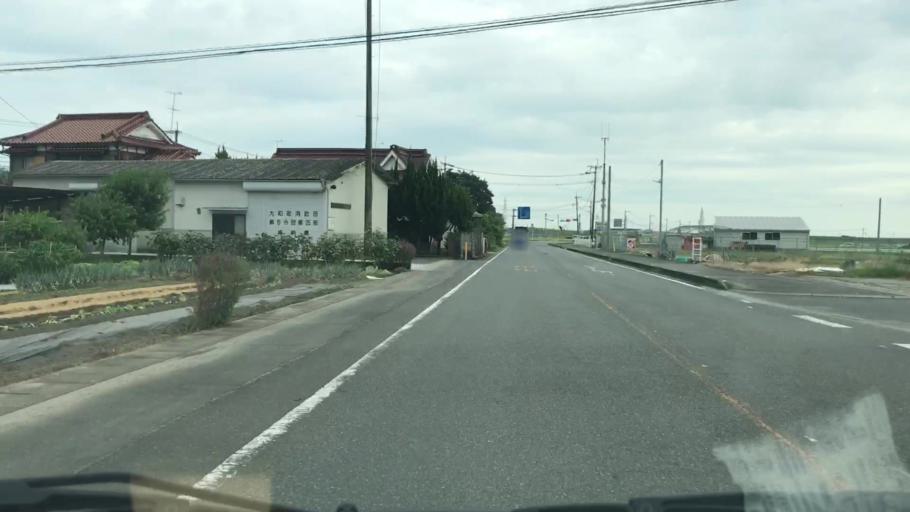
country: JP
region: Saga Prefecture
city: Saga-shi
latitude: 33.2865
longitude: 130.2507
